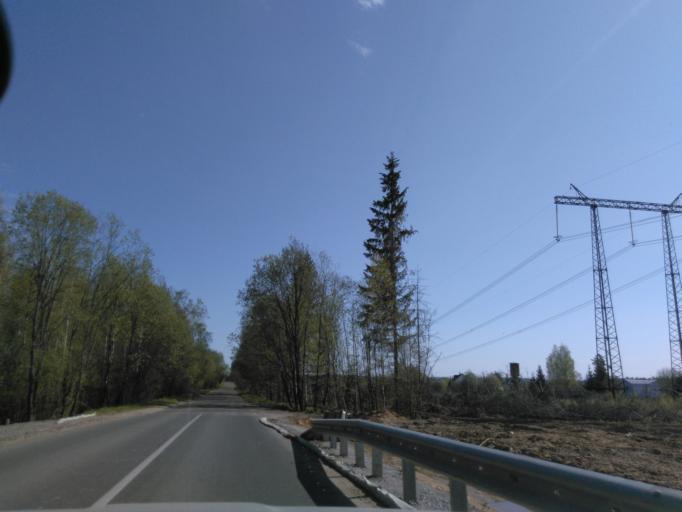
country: RU
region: Moskovskaya
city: Mendeleyevo
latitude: 56.0654
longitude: 37.2394
